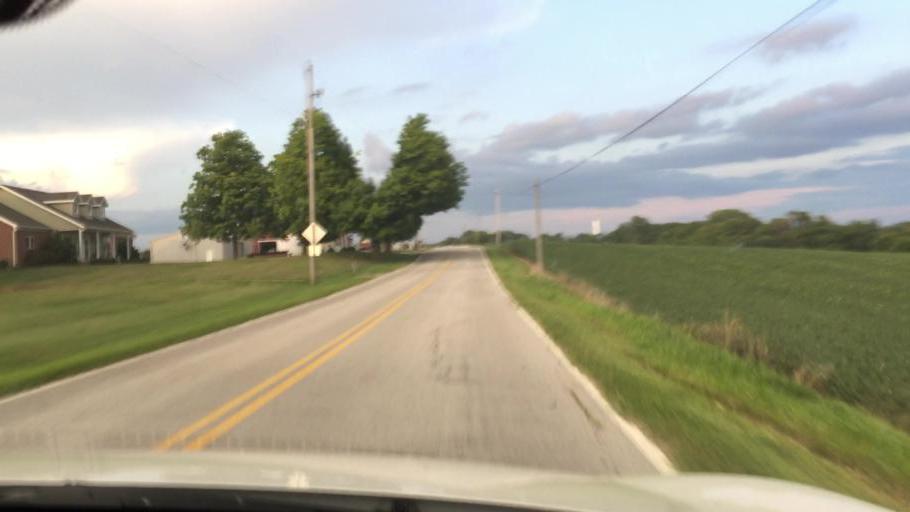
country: US
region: Ohio
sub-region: Champaign County
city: Mechanicsburg
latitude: 39.9967
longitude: -83.6359
